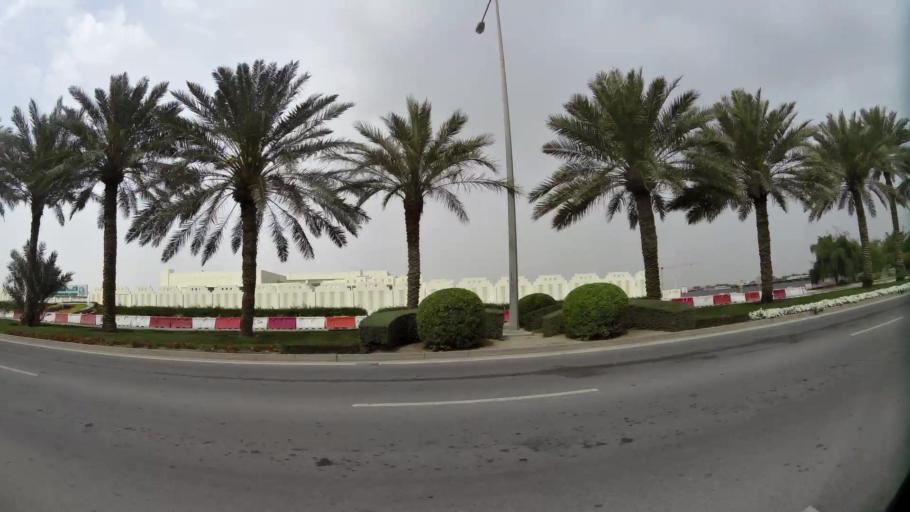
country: QA
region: Baladiyat ad Dawhah
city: Doha
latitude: 25.2880
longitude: 51.4959
